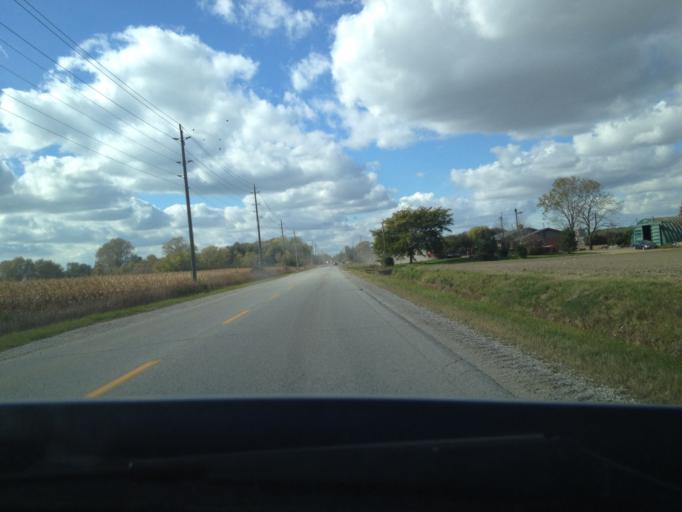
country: CA
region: Ontario
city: Amherstburg
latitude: 42.0329
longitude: -82.5754
